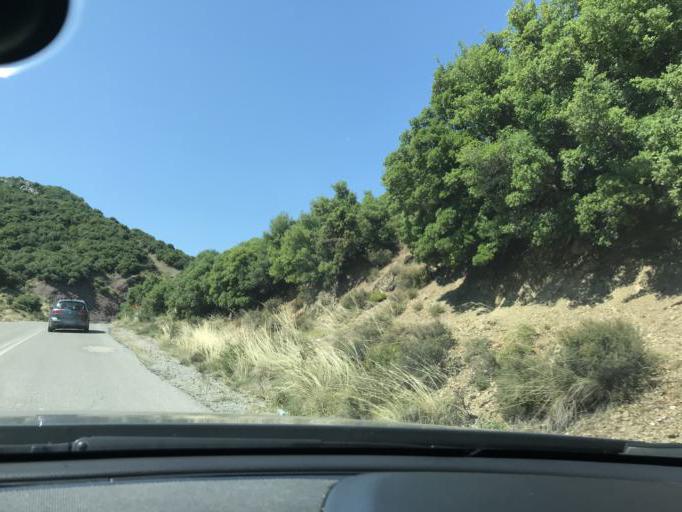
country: GR
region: Central Greece
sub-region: Nomos Voiotias
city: Distomo
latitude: 38.4937
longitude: 22.6972
